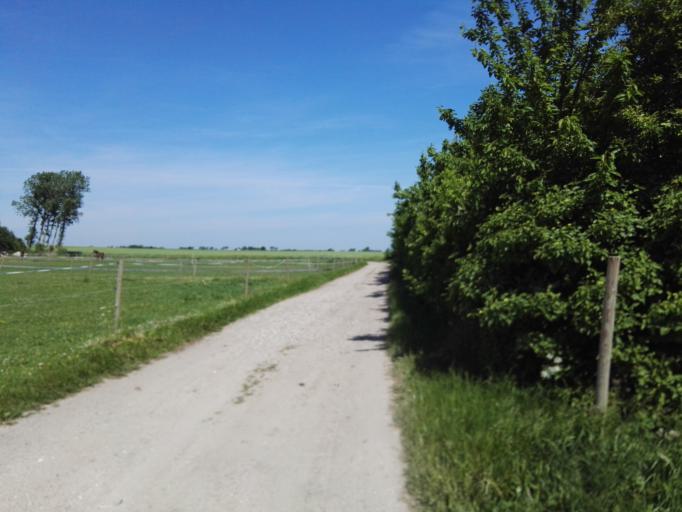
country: DK
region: Capital Region
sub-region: Frederikssund Kommune
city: Jaegerspris
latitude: 55.8041
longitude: 11.9947
